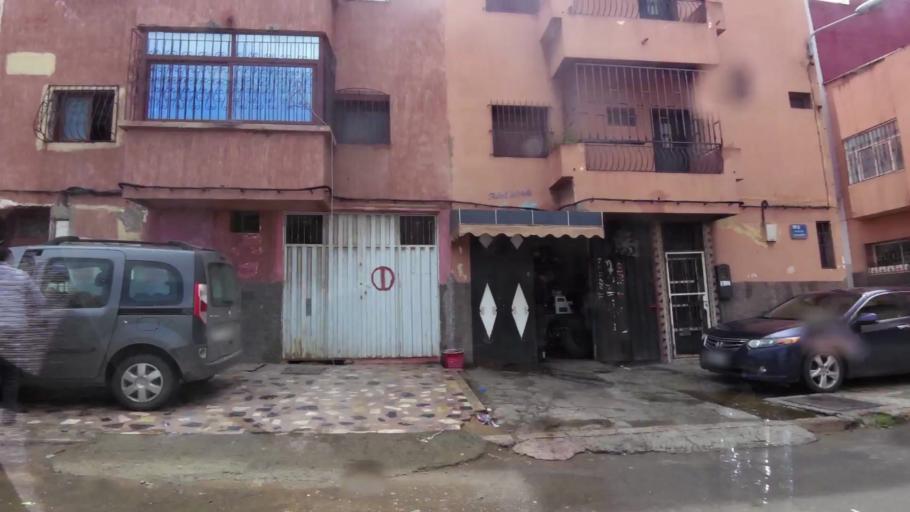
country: MA
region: Grand Casablanca
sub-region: Casablanca
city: Casablanca
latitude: 33.5515
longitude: -7.6883
